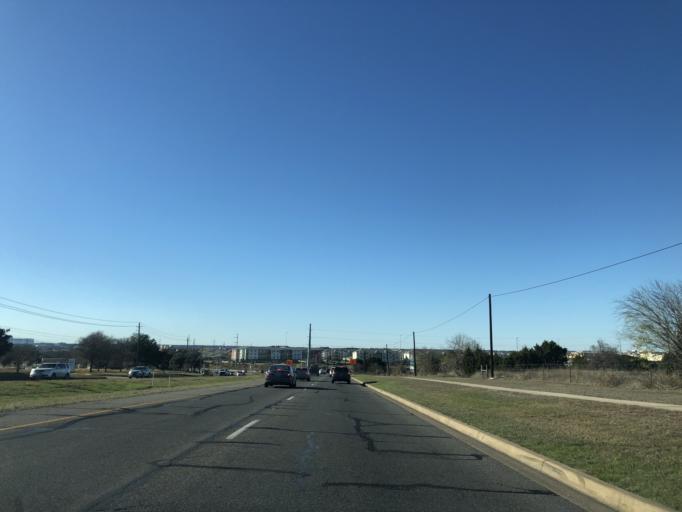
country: US
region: Texas
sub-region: Travis County
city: Wells Branch
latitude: 30.4043
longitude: -97.6608
